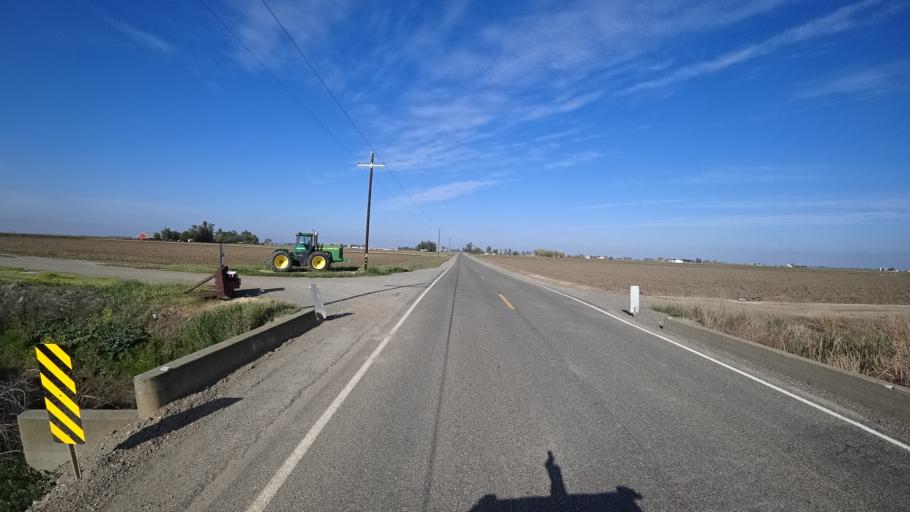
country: US
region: California
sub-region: Glenn County
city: Hamilton City
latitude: 39.5825
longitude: -122.0180
